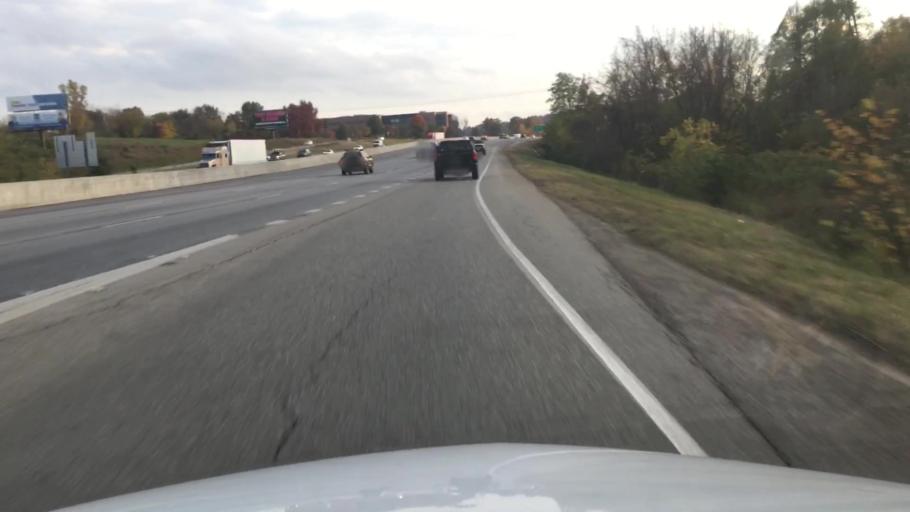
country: US
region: Arkansas
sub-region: Benton County
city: Lowell
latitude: 36.2505
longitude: -94.1507
